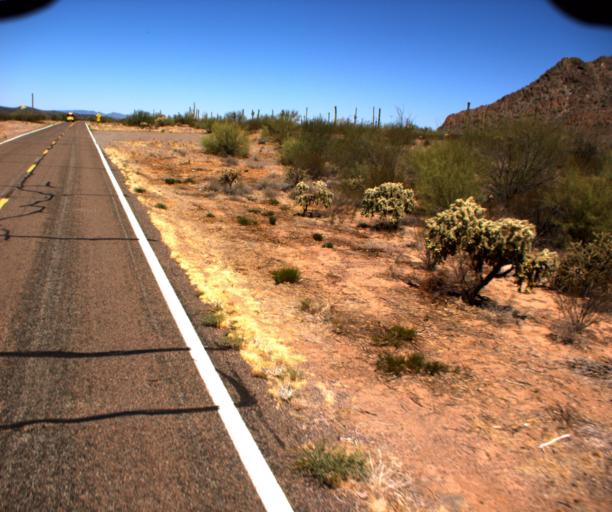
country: US
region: Arizona
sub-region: Pima County
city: Ajo
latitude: 32.2224
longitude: -112.6924
